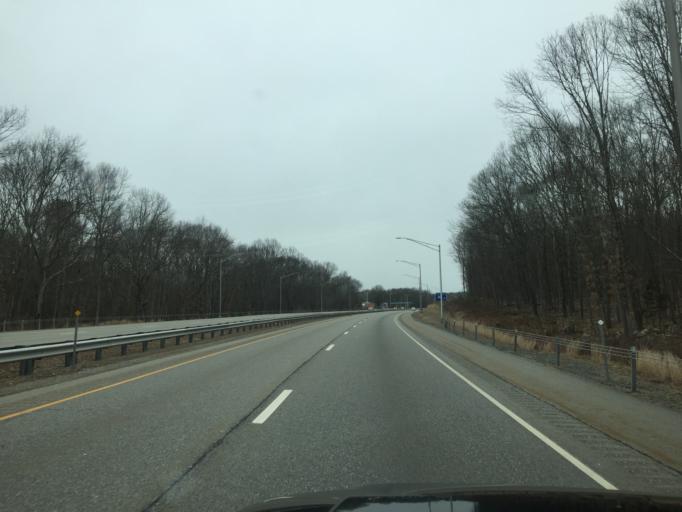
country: US
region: Connecticut
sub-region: Windham County
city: Wauregan
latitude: 41.7493
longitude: -71.8792
